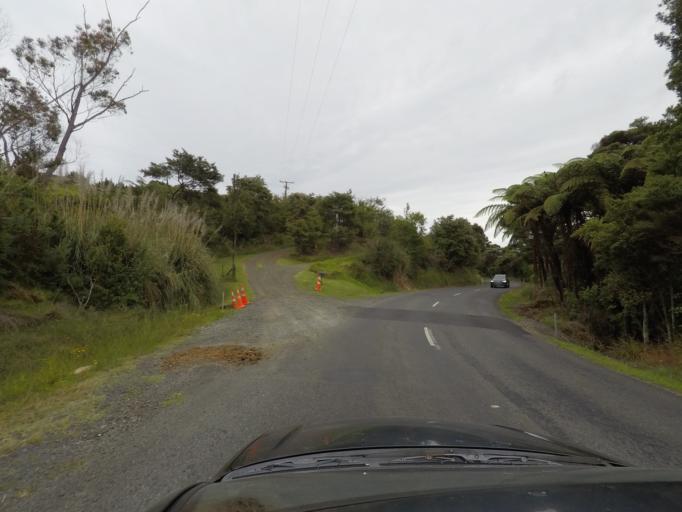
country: NZ
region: Waikato
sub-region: Waikato District
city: Raglan
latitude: -37.8261
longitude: 174.8153
